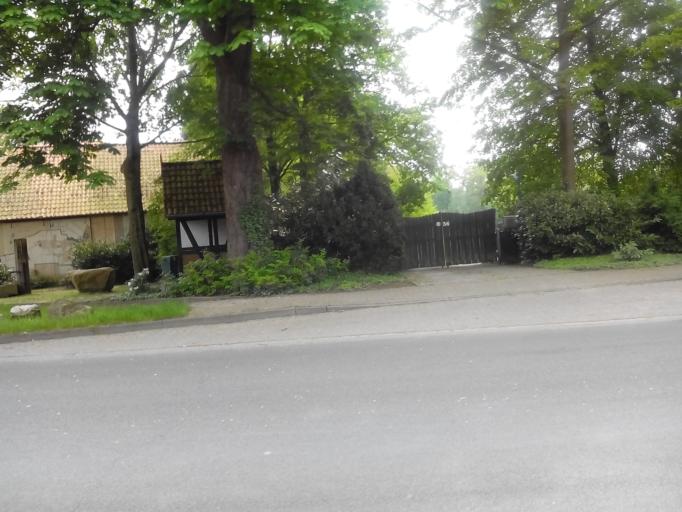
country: DE
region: Lower Saxony
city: Verden
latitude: 52.9198
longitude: 9.2577
